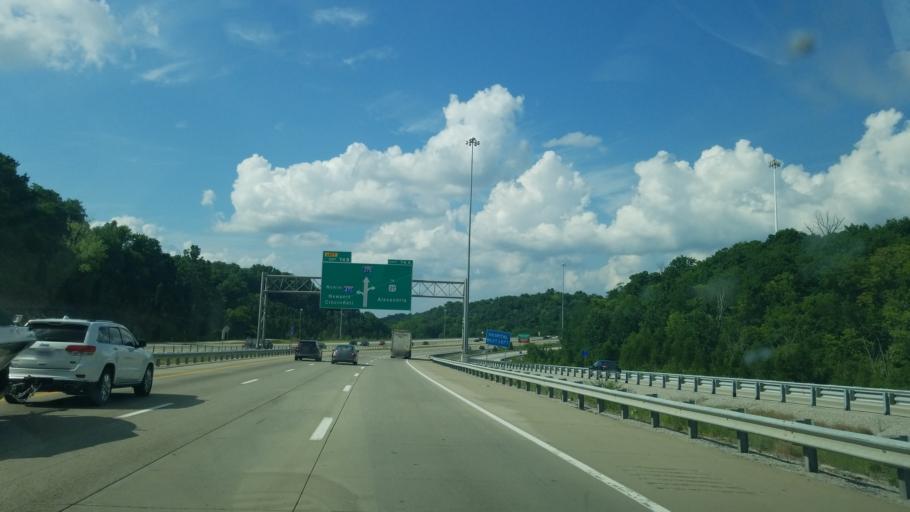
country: US
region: Kentucky
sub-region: Campbell County
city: Highland Heights
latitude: 39.0391
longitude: -84.4700
